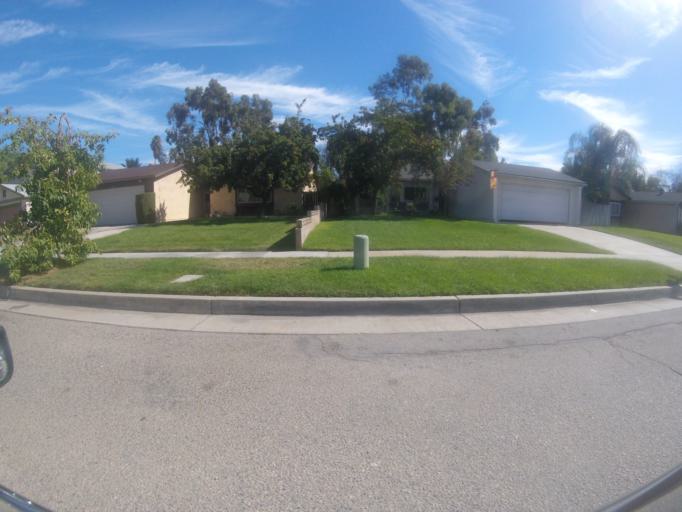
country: US
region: California
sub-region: San Bernardino County
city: Redlands
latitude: 34.0612
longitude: -117.1595
